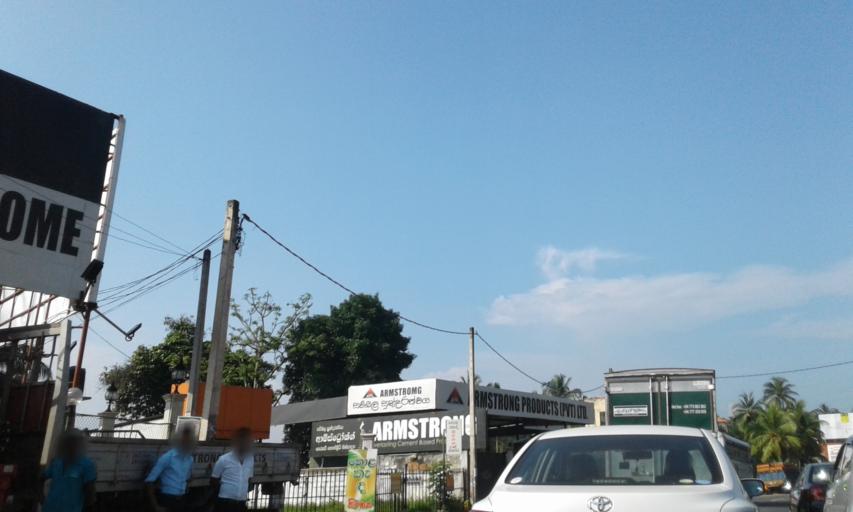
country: LK
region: Western
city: Welisara
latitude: 7.0146
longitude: 79.9689
